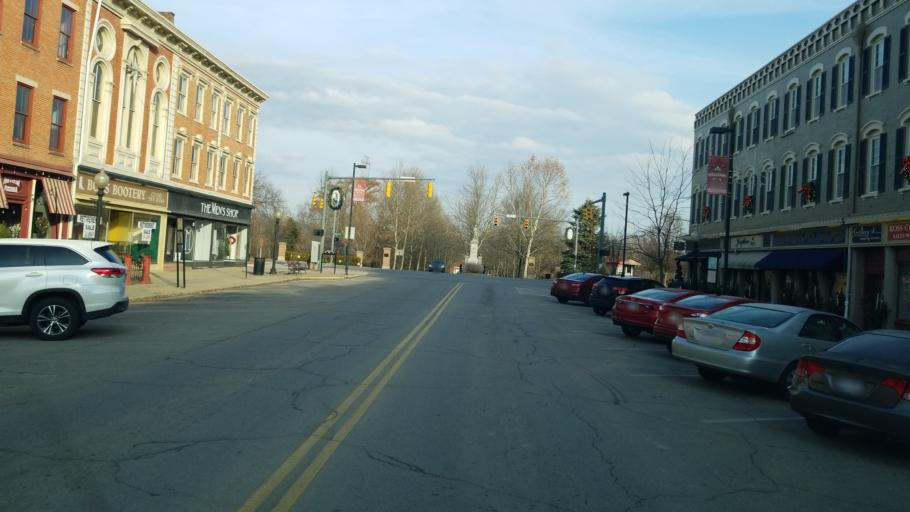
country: US
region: Ohio
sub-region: Ross County
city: Chillicothe
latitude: 39.3352
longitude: -82.9827
